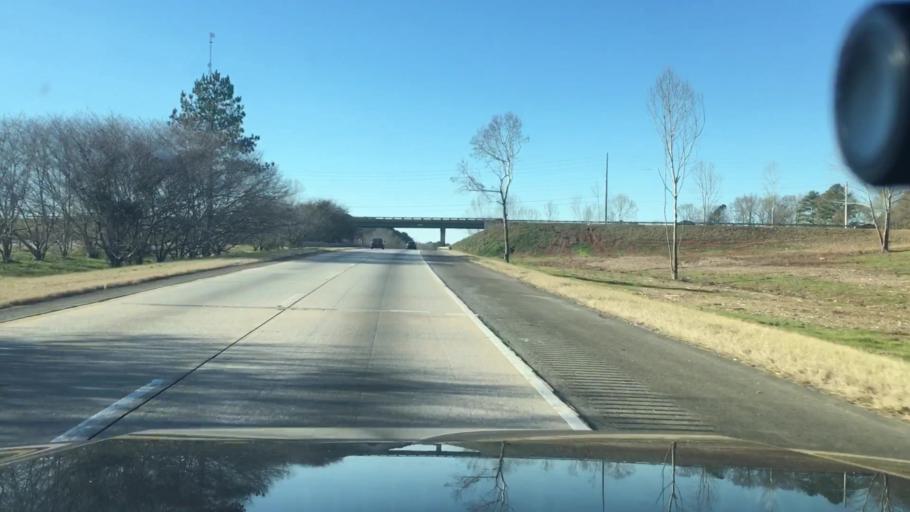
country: US
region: Georgia
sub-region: Bibb County
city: Macon
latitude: 32.9274
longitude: -83.7295
